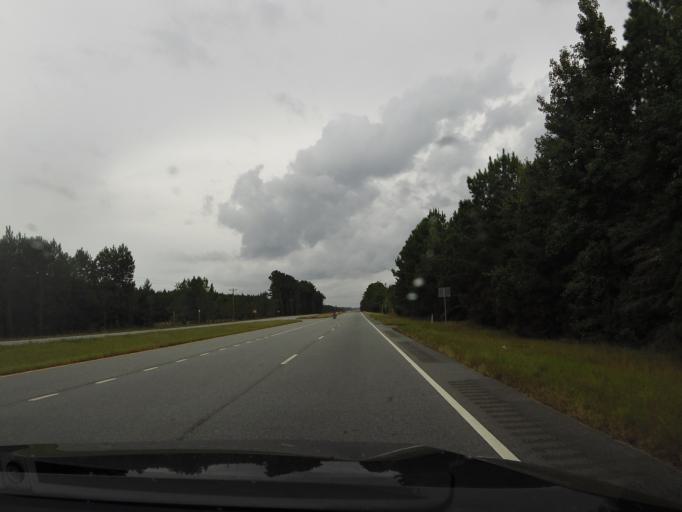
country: US
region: Georgia
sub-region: McIntosh County
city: Darien
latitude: 31.3981
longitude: -81.6482
